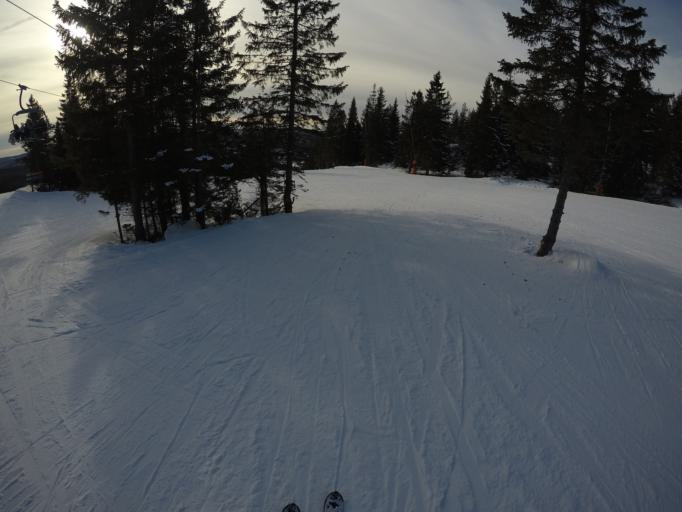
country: SE
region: Dalarna
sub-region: Borlange Kommun
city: Borlaenge
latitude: 60.3807
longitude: 15.4180
